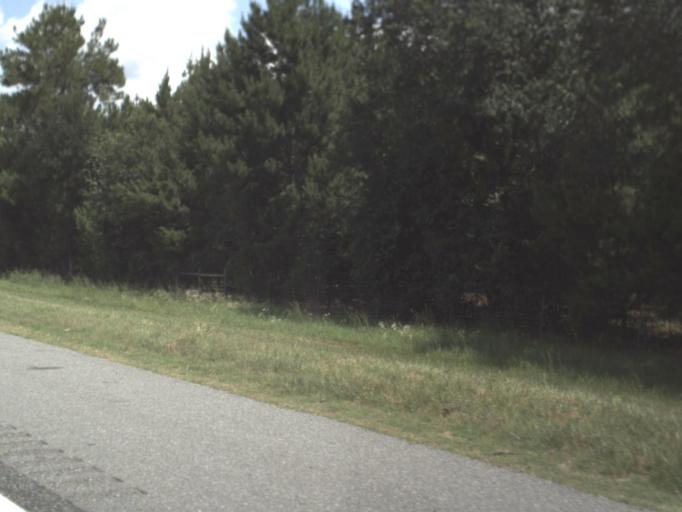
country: US
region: Florida
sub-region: Suwannee County
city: Wellborn
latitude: 30.2822
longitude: -82.7658
